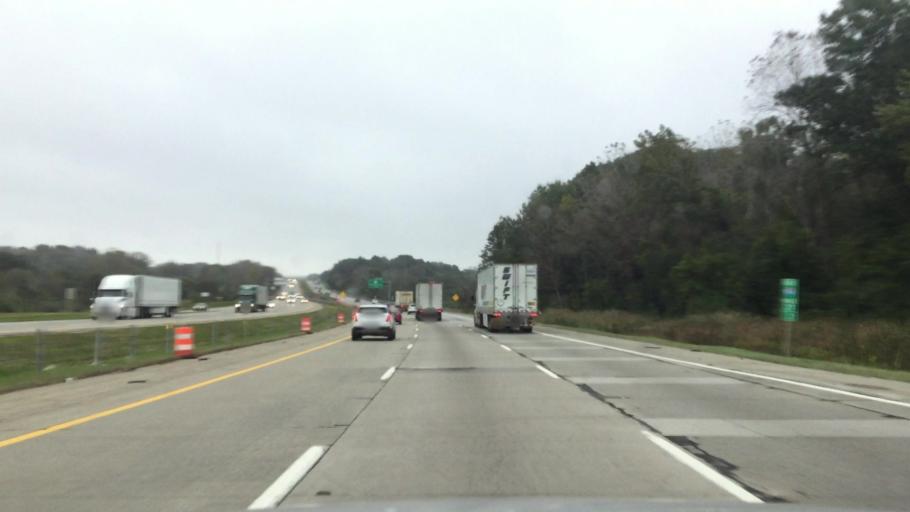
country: US
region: Michigan
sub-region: Berrien County
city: Fair Plain
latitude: 42.0596
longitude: -86.4540
